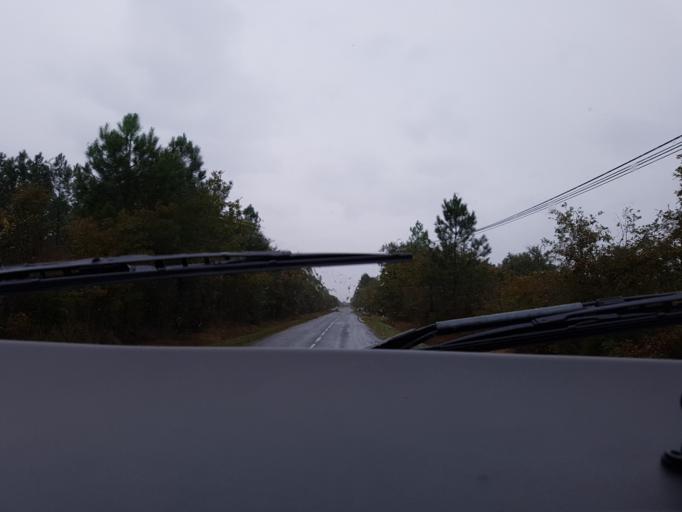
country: FR
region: Aquitaine
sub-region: Departement de la Gironde
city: Saint-Symphorien
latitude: 44.3341
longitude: -0.5963
